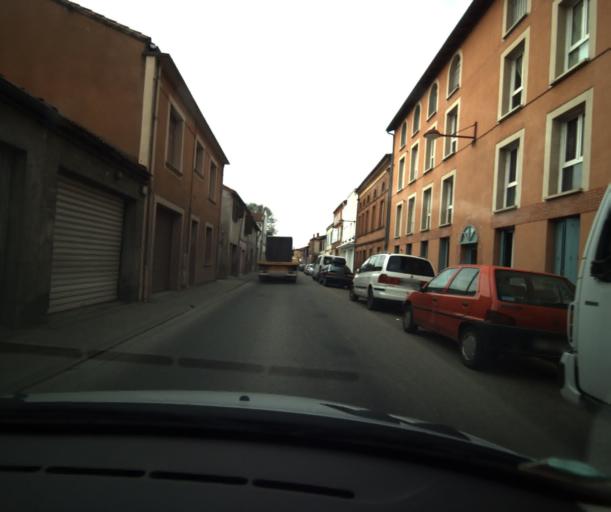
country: FR
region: Midi-Pyrenees
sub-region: Departement du Tarn-et-Garonne
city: Castelsarrasin
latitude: 44.0408
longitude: 1.1073
